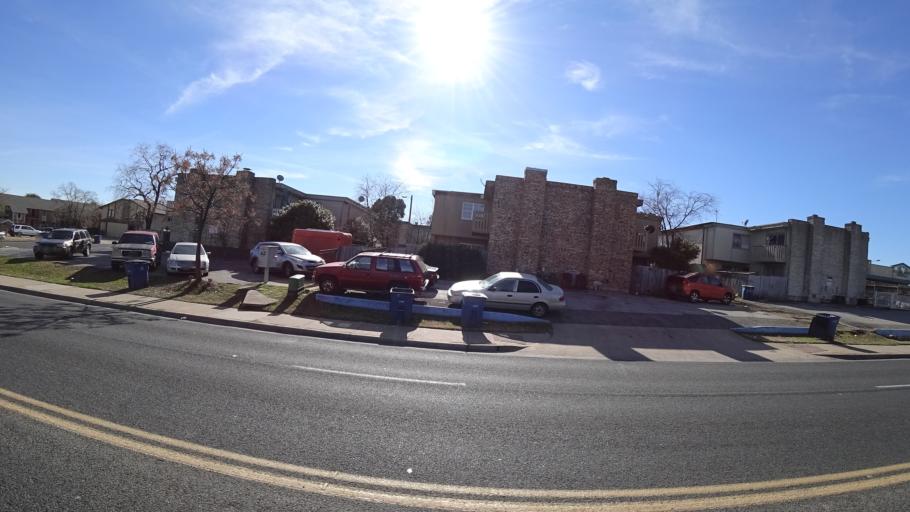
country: US
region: Texas
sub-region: Travis County
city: Wells Branch
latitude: 30.3687
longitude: -97.7044
